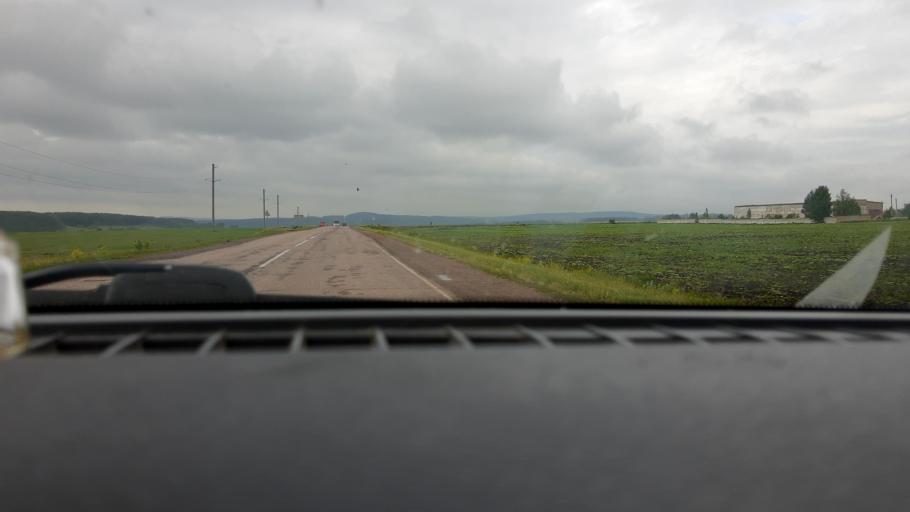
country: RU
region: Bashkortostan
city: Priyutovo
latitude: 53.9676
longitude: 53.9800
